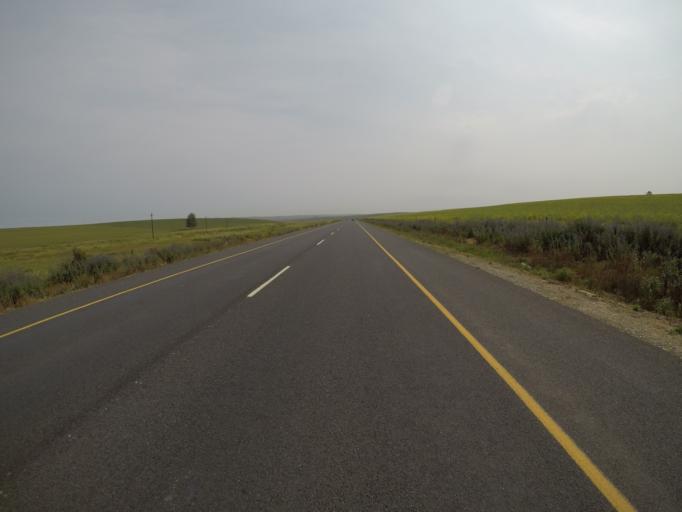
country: ZA
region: Western Cape
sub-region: West Coast District Municipality
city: Malmesbury
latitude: -33.4680
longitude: 18.7915
